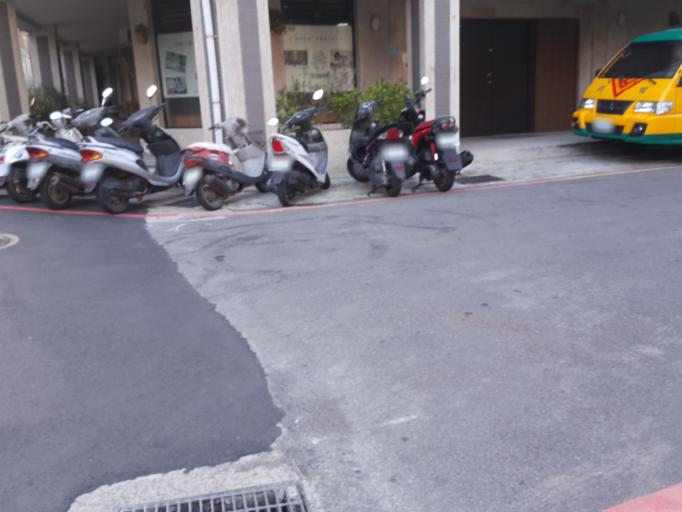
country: TW
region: Taiwan
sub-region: Hsinchu
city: Hsinchu
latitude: 24.8064
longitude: 120.9668
